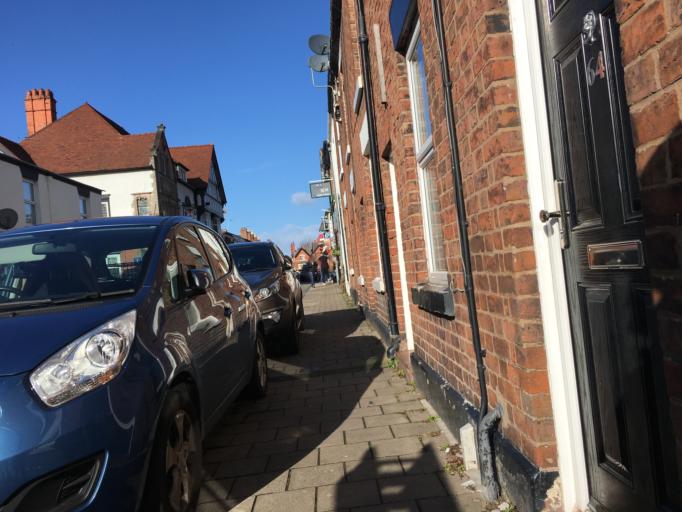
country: GB
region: England
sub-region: Cheshire West and Chester
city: Hoole
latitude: 53.1986
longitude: -2.8758
